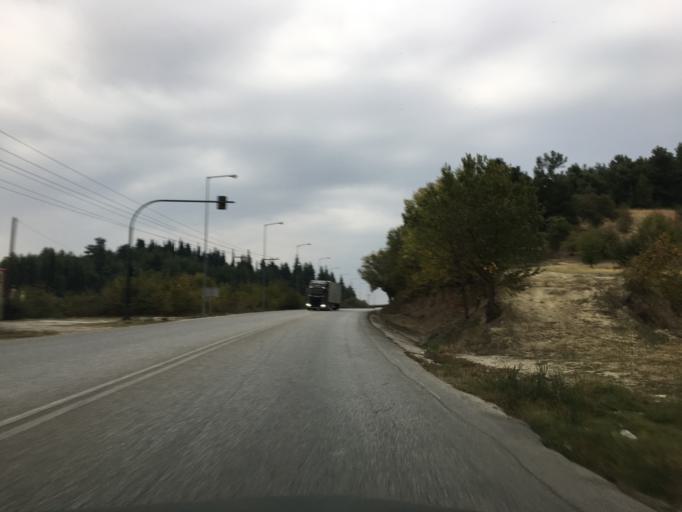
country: GR
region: Thessaly
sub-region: Trikala
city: Trikala
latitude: 39.5696
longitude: 21.7626
